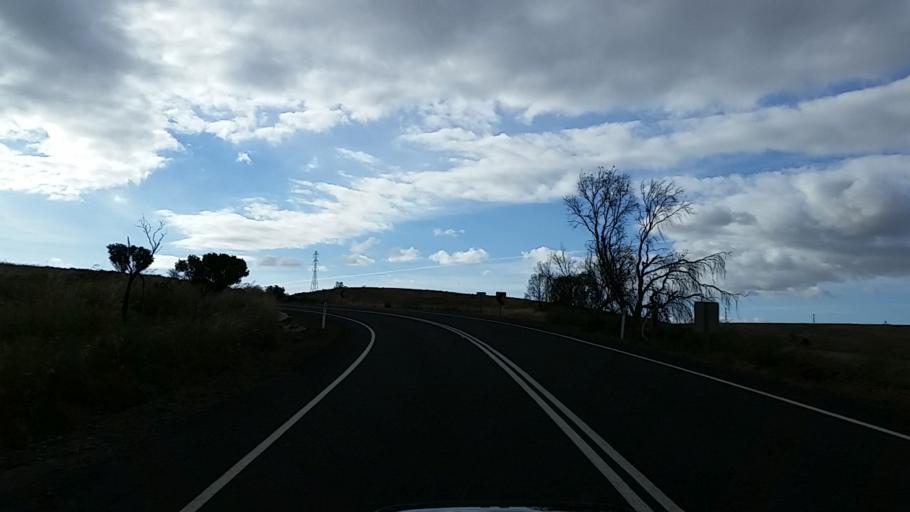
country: AU
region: South Australia
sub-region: Barossa
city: Angaston
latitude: -34.5610
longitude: 139.2035
